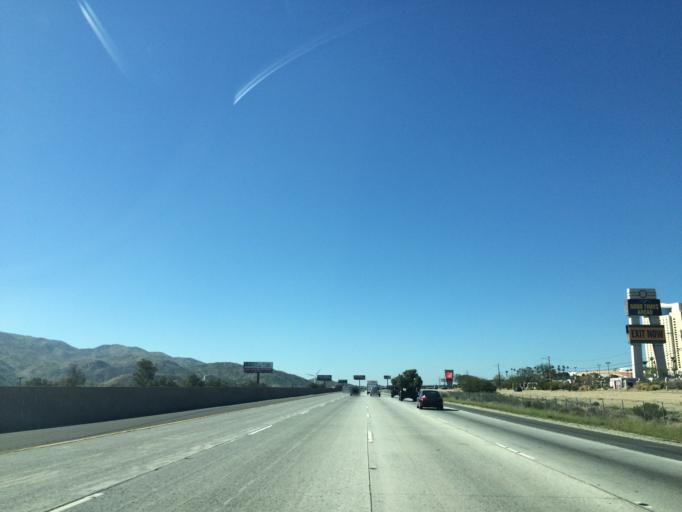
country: US
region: California
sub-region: Riverside County
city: Cabazon
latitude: 33.9189
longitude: -116.7921
